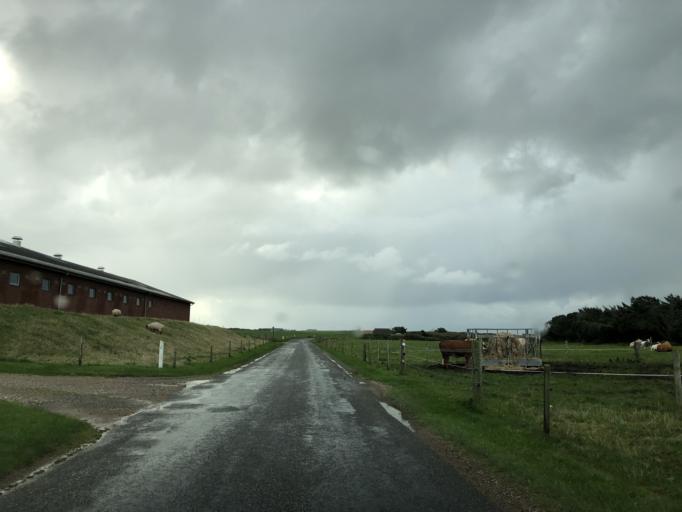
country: DK
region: Central Jutland
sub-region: Lemvig Kommune
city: Harboore
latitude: 56.5457
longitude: 8.1387
